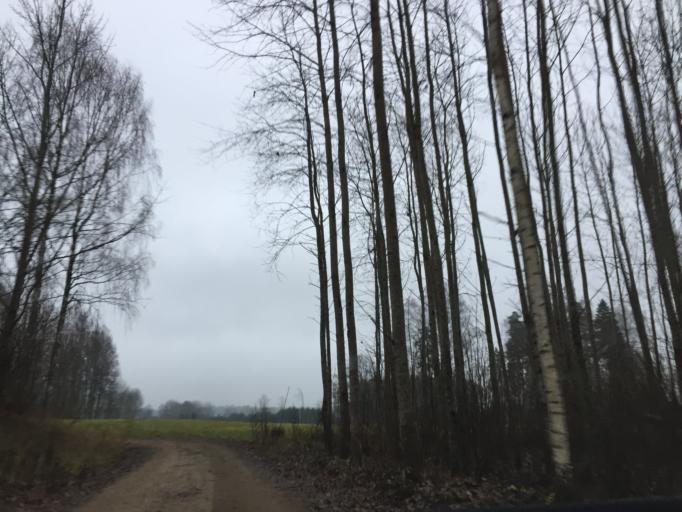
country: LV
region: Koceni
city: Koceni
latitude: 57.5342
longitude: 25.3404
